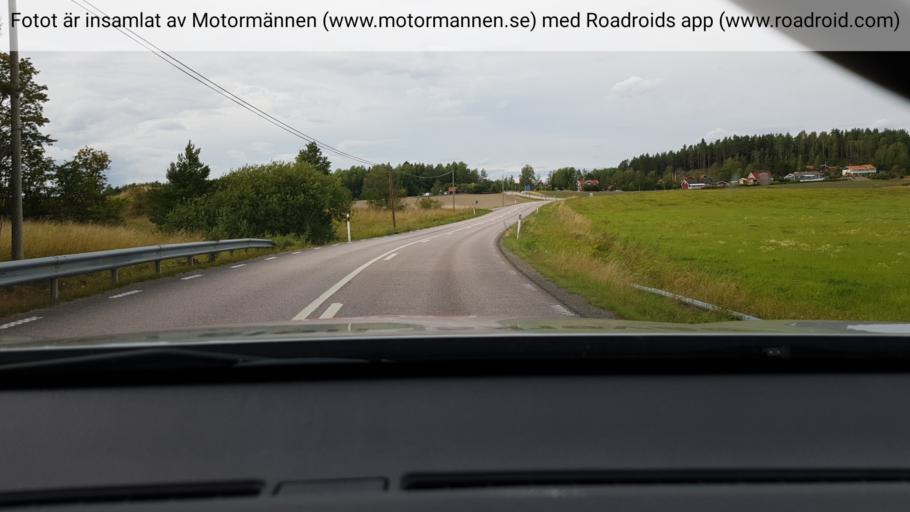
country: SE
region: Soedermanland
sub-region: Gnesta Kommun
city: Gnesta
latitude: 59.0600
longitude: 17.1765
